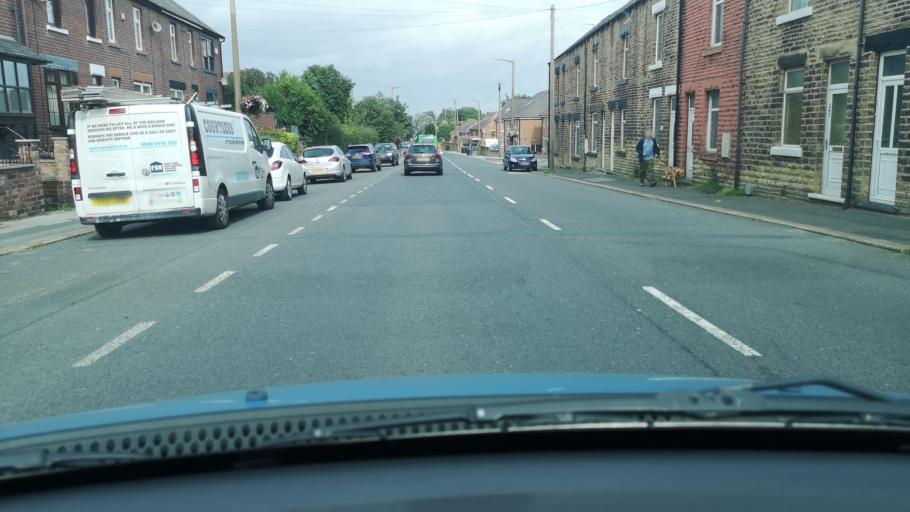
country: GB
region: England
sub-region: Barnsley
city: Shafton
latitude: 53.5856
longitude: -1.4102
